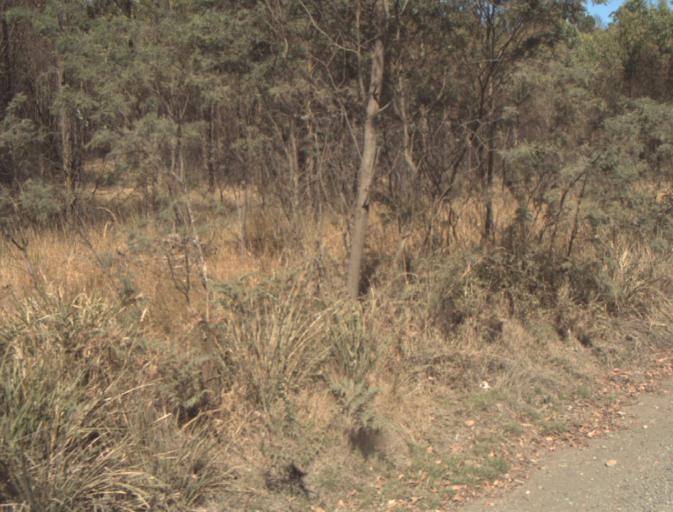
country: AU
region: Tasmania
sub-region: Launceston
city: Newstead
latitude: -41.3788
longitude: 147.2913
